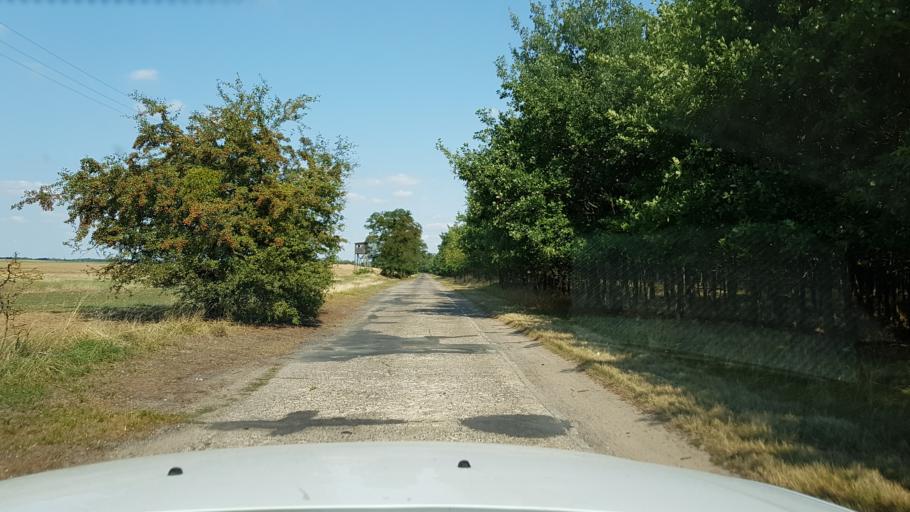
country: PL
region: West Pomeranian Voivodeship
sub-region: Powiat gryfinski
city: Moryn
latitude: 52.8309
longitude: 14.3713
